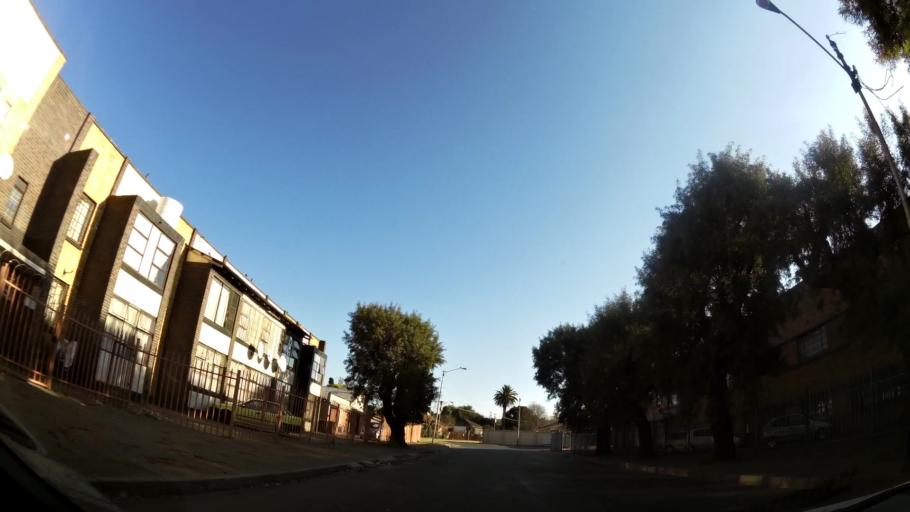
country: ZA
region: Gauteng
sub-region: Ekurhuleni Metropolitan Municipality
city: Germiston
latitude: -26.1964
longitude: 28.1476
